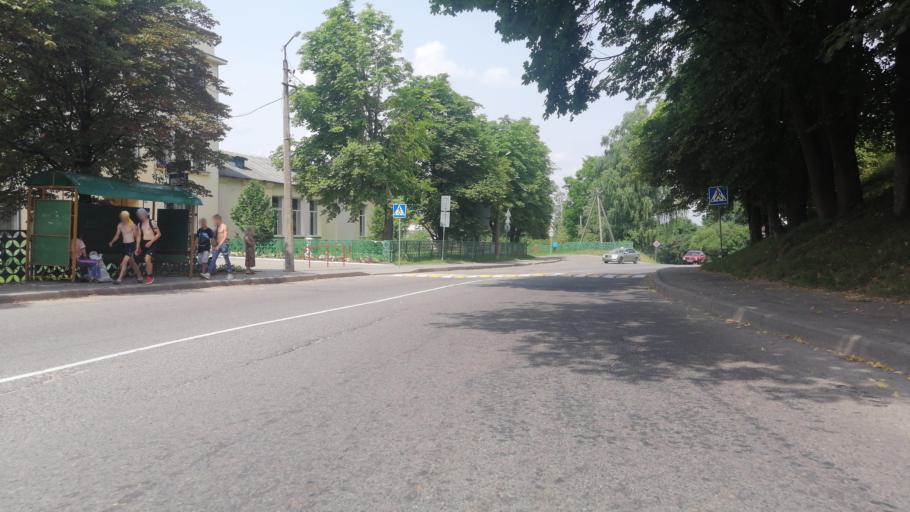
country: BY
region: Grodnenskaya
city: Navahrudak
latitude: 53.6016
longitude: 25.8236
